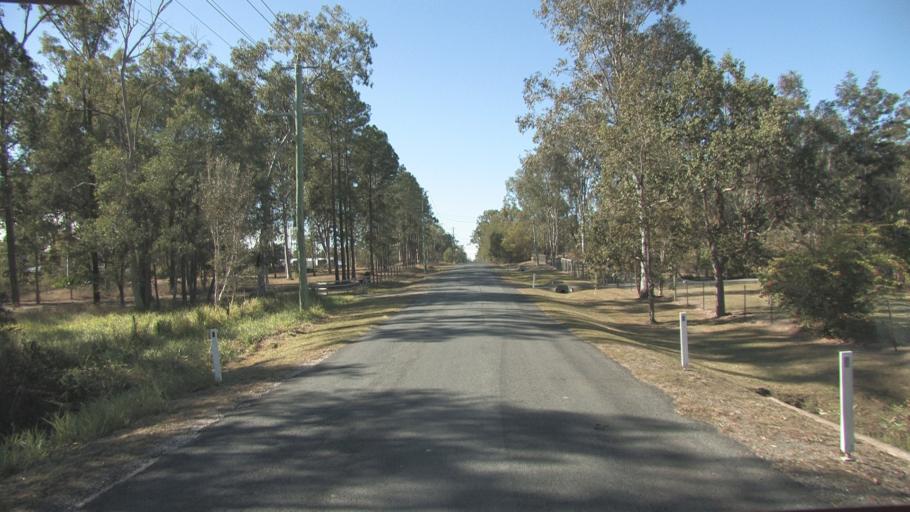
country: AU
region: Queensland
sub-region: Logan
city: North Maclean
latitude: -27.7984
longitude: 153.0448
